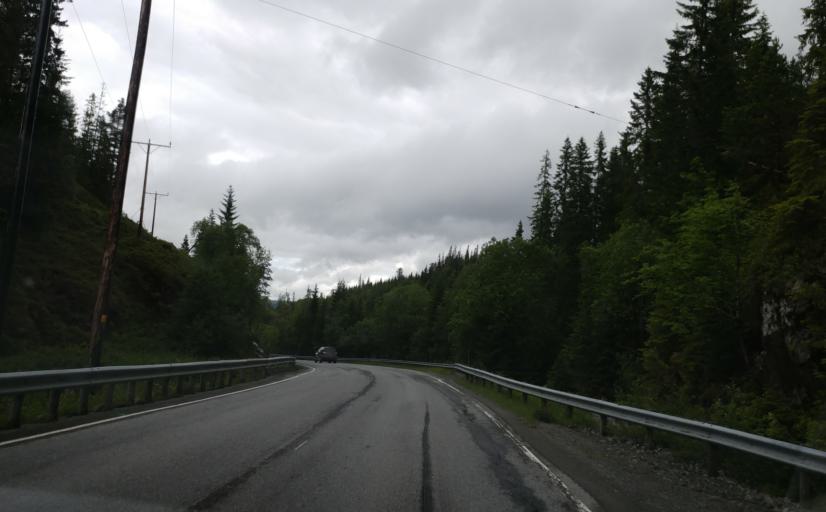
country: NO
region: Sor-Trondelag
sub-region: Selbu
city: Mebonden
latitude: 63.3593
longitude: 11.0779
